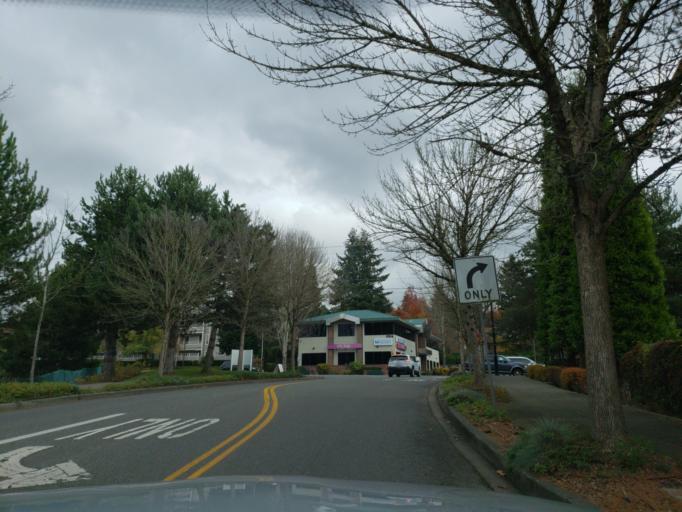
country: US
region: Washington
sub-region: King County
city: Woodinville
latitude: 47.7578
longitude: -122.1536
